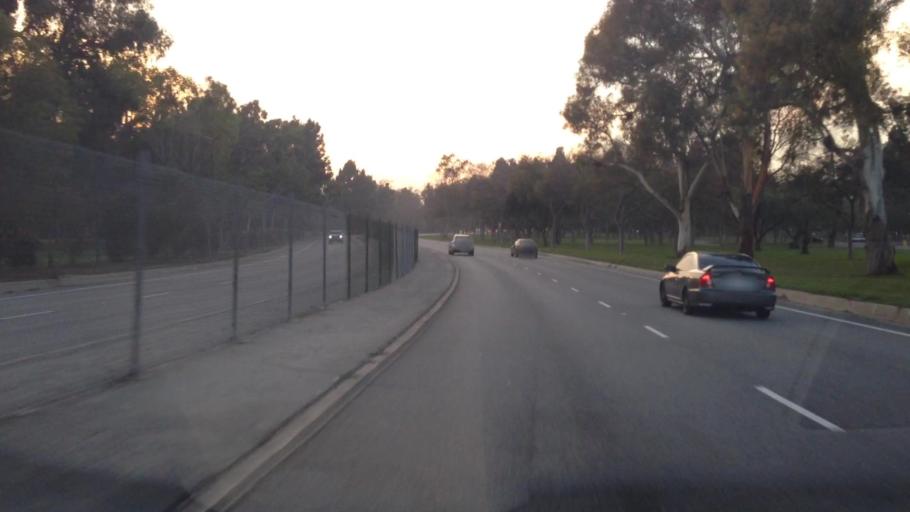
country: US
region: California
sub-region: Orange County
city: Rossmoor
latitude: 33.8042
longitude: -118.0931
